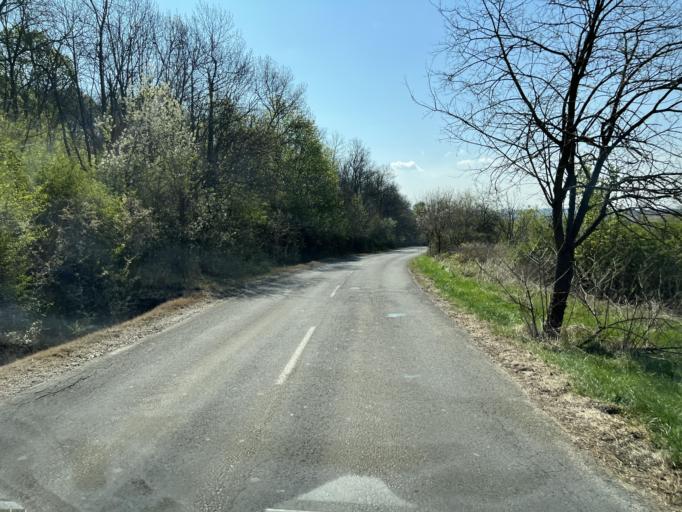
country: HU
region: Pest
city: Orbottyan
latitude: 47.7381
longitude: 19.2942
